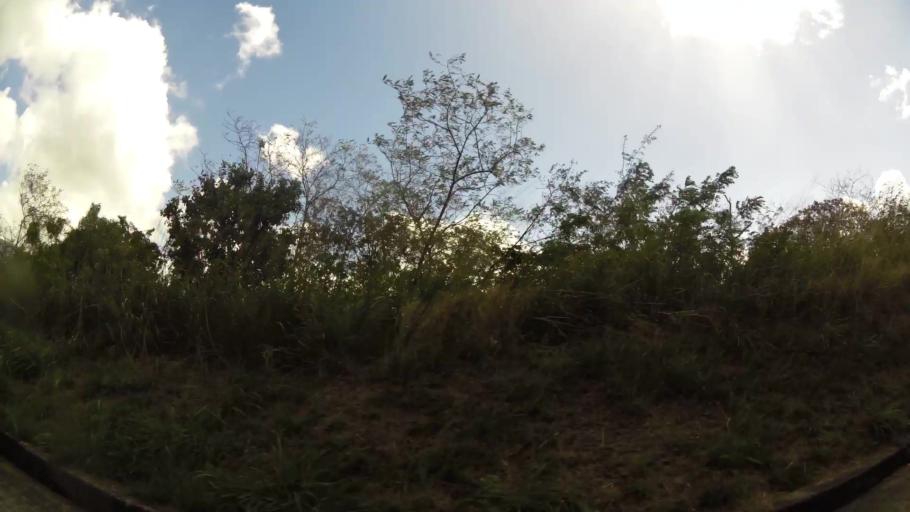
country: MQ
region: Martinique
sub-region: Martinique
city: Saint-Pierre
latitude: 14.6944
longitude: -61.1695
